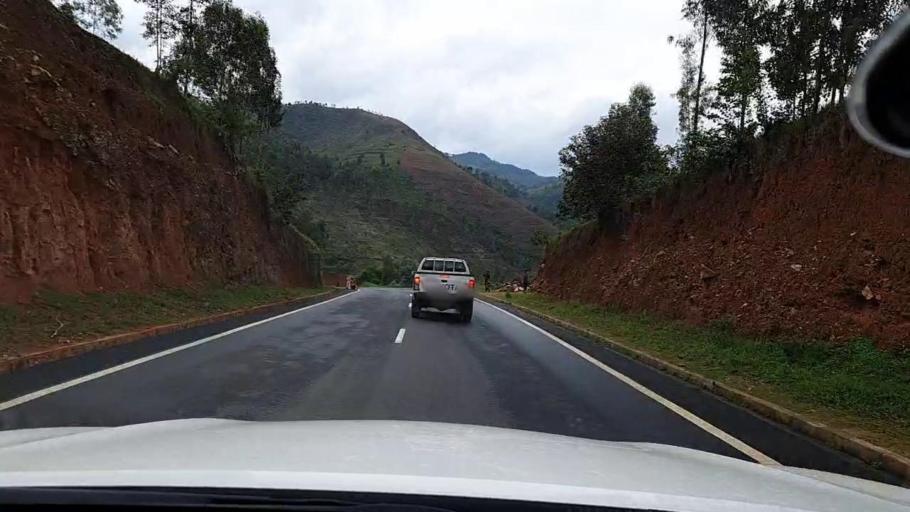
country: RW
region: Western Province
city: Kibuye
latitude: -2.1644
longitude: 29.2964
